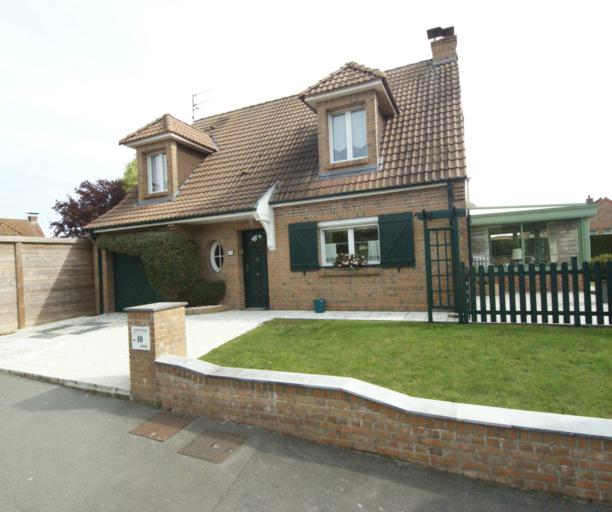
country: FR
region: Nord-Pas-de-Calais
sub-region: Departement du Nord
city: Radinghem-en-Weppes
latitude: 50.6141
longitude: 2.9308
